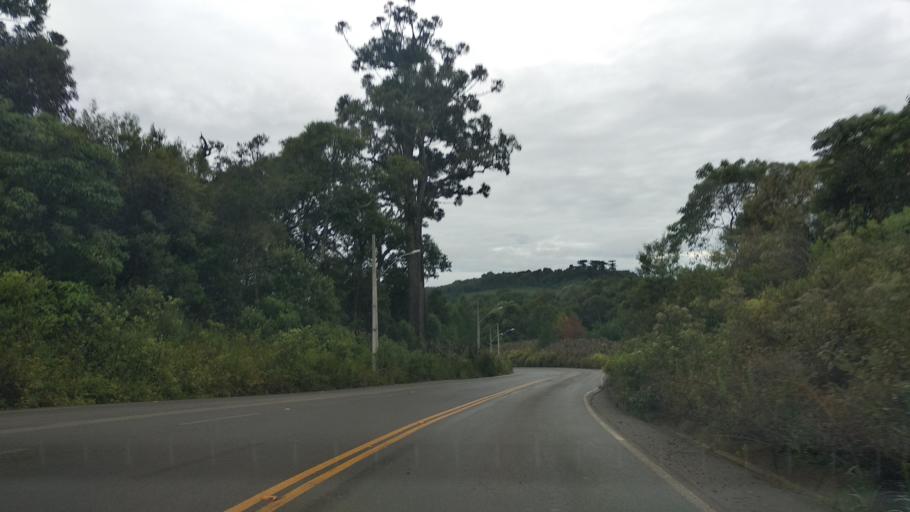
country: BR
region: Santa Catarina
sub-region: Videira
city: Videira
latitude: -27.0309
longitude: -51.1565
